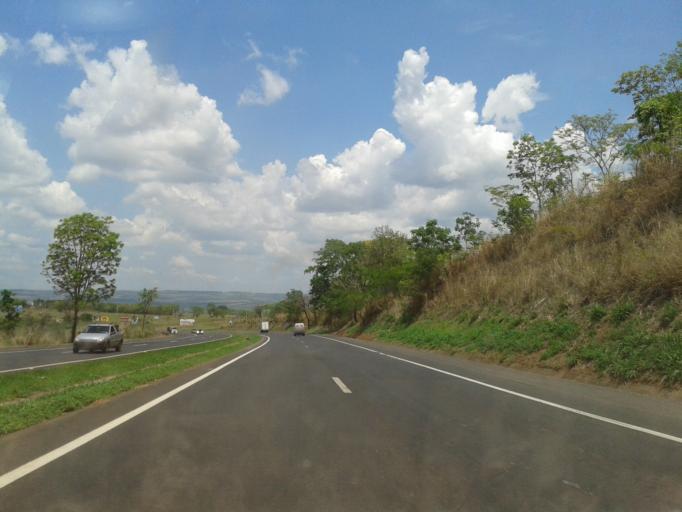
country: BR
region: Minas Gerais
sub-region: Araguari
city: Araguari
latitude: -18.7299
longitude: -48.2205
